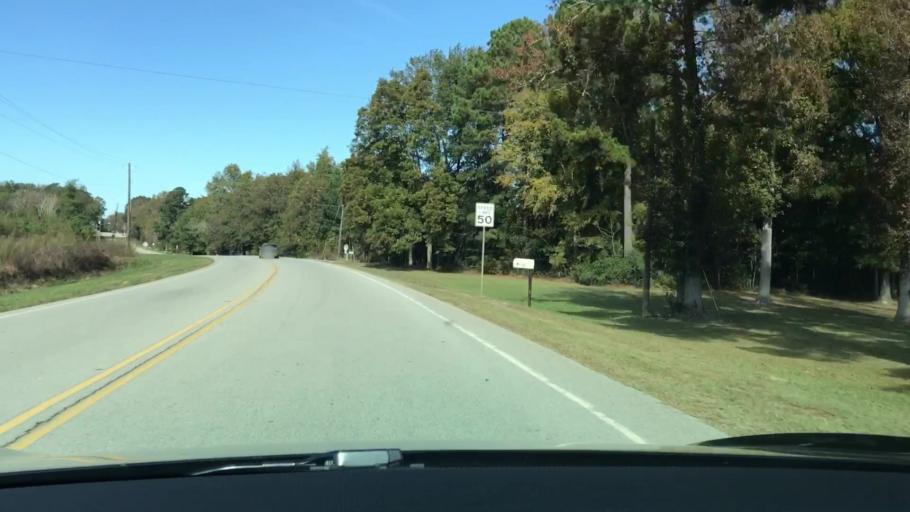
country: US
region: Georgia
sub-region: Warren County
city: Firing Range
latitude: 33.4575
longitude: -82.6995
